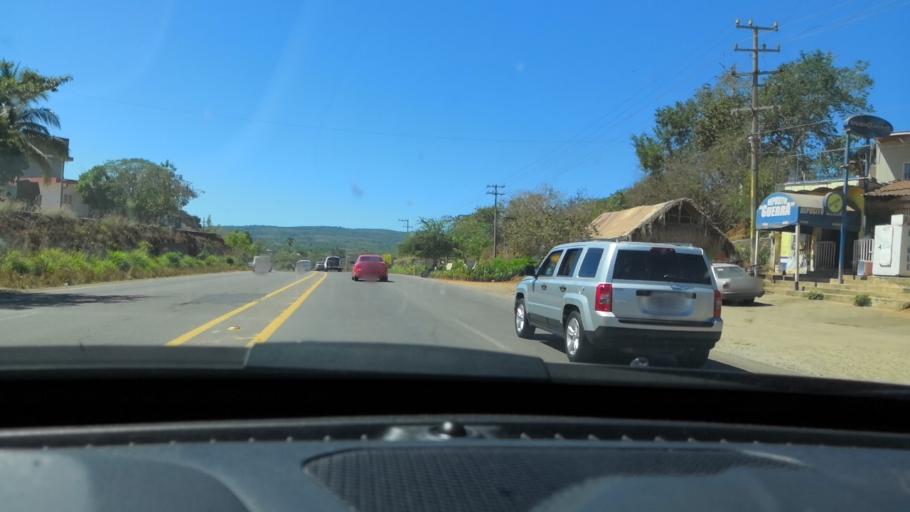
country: MX
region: Nayarit
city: Las Varas
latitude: 21.1758
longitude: -105.1428
